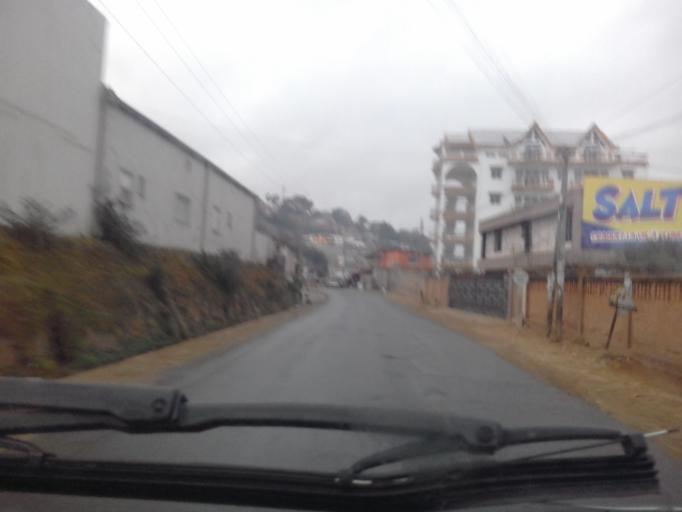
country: MG
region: Analamanga
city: Antananarivo
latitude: -18.8685
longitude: 47.5512
